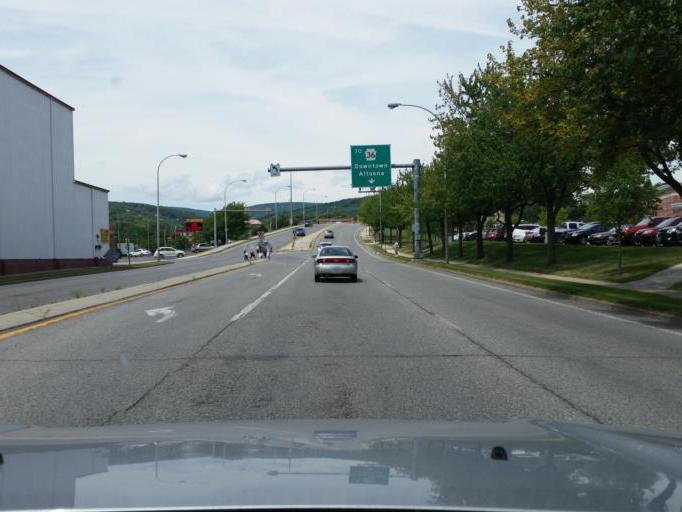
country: US
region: Pennsylvania
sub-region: Blair County
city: Altoona
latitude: 40.5104
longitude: -78.4034
